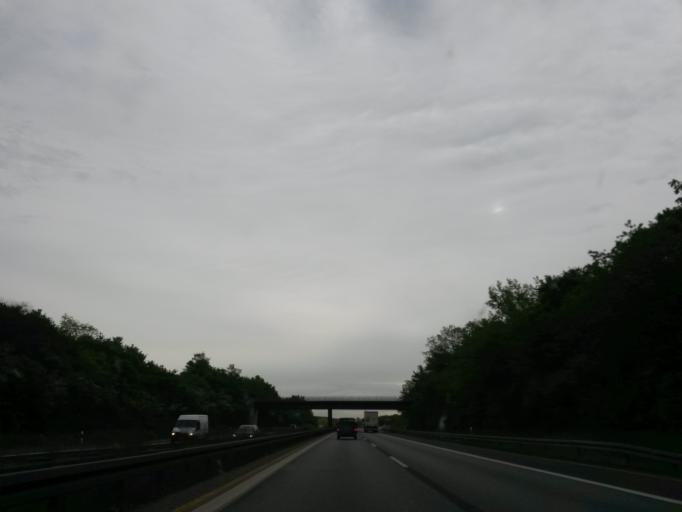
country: DE
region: Bavaria
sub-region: Regierungsbezirk Unterfranken
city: Dettelbach
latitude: 49.7879
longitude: 10.1668
